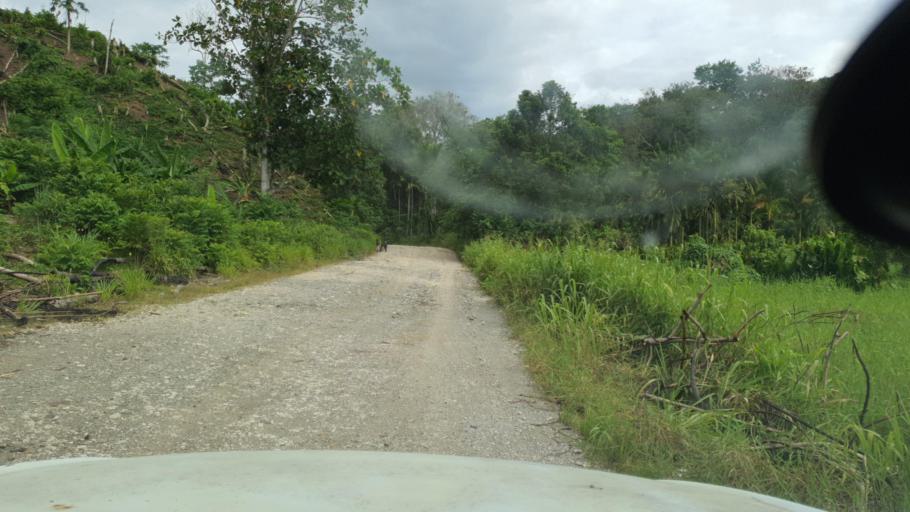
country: SB
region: Guadalcanal
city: Honiara
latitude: -9.4757
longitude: 160.0418
